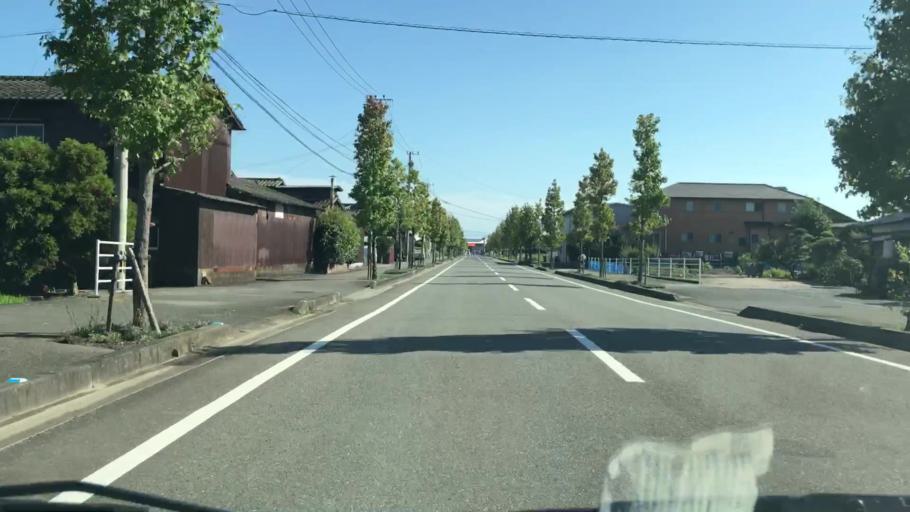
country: JP
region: Saga Prefecture
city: Okawa
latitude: 33.1853
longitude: 130.3138
